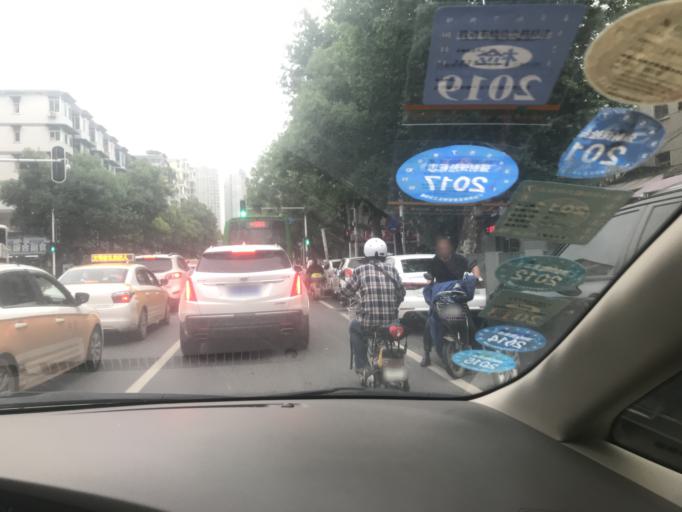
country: CN
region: Hubei
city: Wuhan
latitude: 30.5520
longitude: 114.2642
